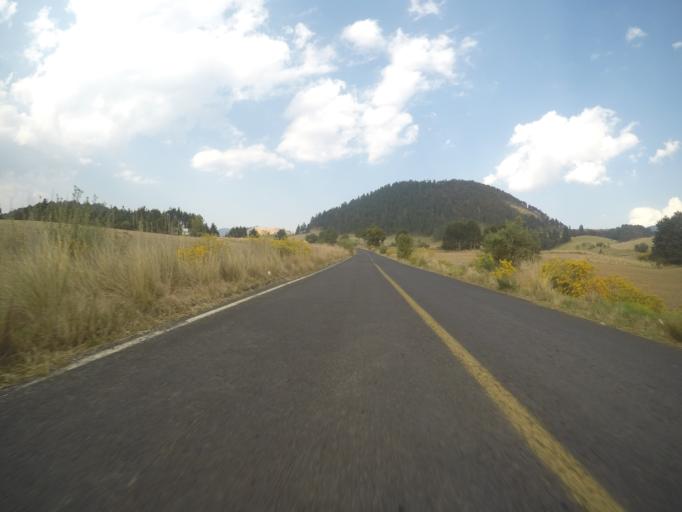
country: MX
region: Mexico
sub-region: Xalatlaco
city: San Juan Tomasquillo Herradura
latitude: 19.1628
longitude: -99.3881
